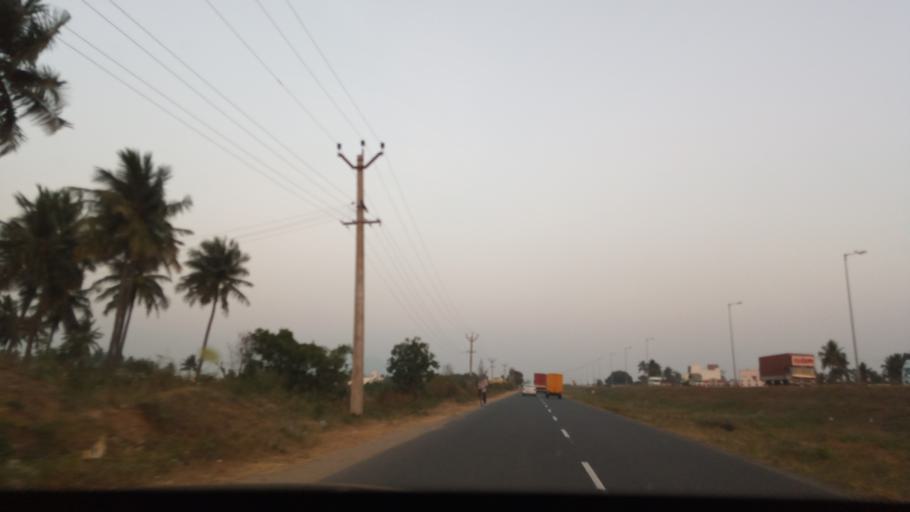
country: IN
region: Tamil Nadu
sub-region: Salem
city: Salem
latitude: 11.6643
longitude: 78.2366
